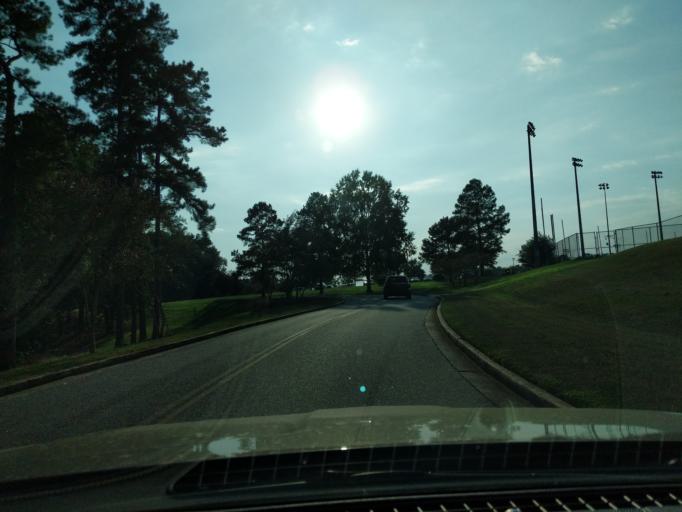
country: US
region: South Carolina
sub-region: Aiken County
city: North Augusta
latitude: 33.5001
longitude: -81.9823
